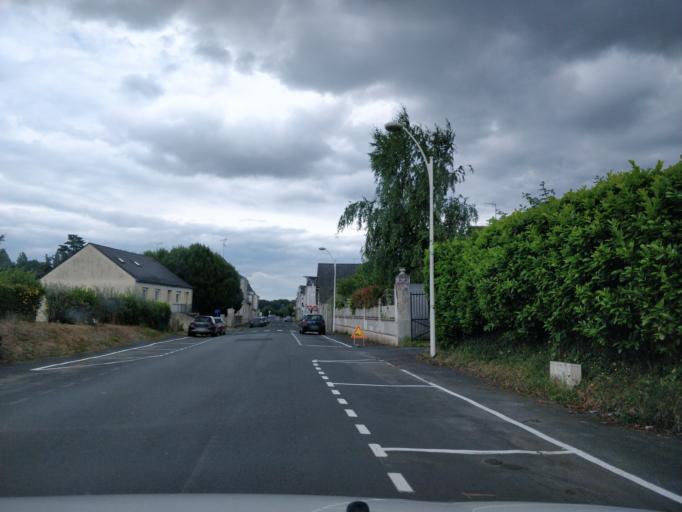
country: FR
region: Pays de la Loire
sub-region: Departement de Maine-et-Loire
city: Grez-Neuville
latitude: 47.6303
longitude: -0.7160
